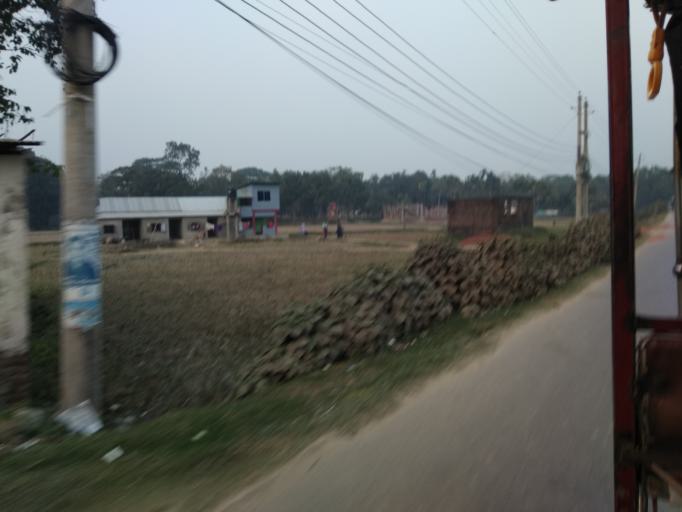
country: BD
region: Dhaka
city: Netrakona
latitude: 24.8687
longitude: 90.7063
